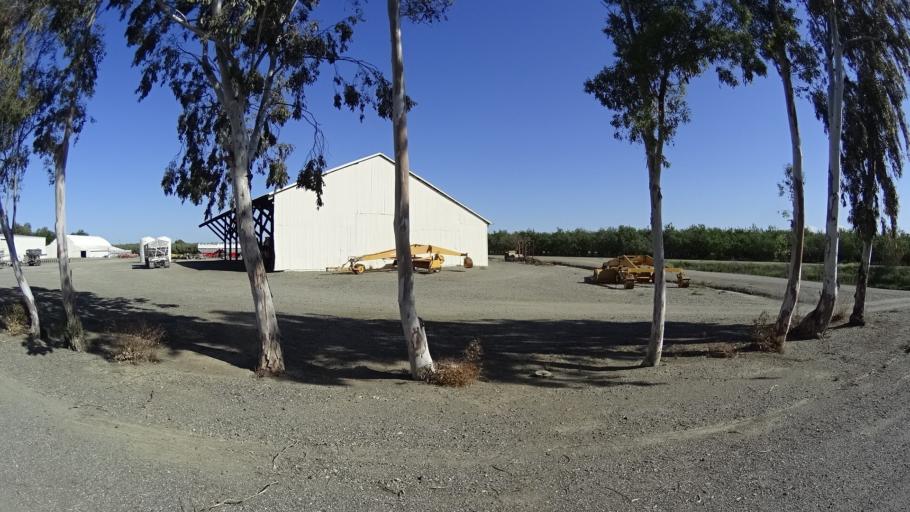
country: US
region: California
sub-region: Glenn County
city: Hamilton City
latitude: 39.6782
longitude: -122.0710
